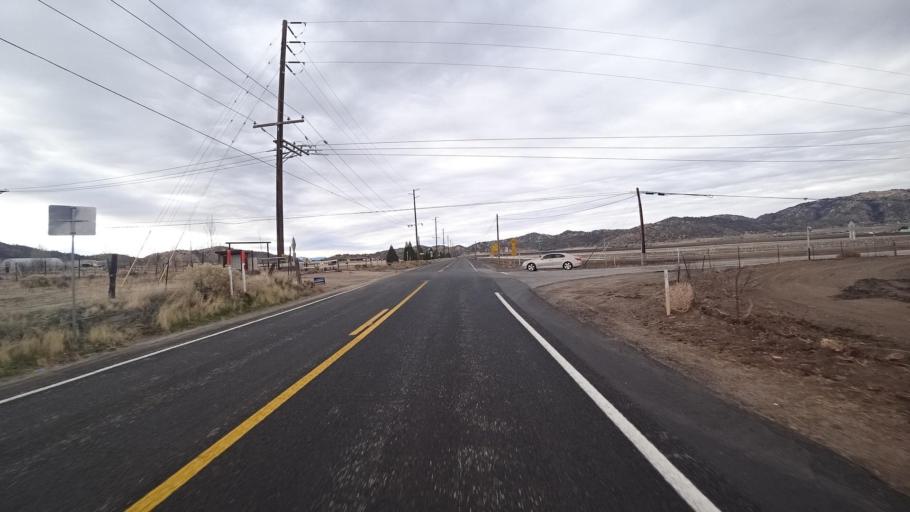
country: US
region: California
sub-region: Kern County
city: Stallion Springs
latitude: 35.0946
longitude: -118.6019
